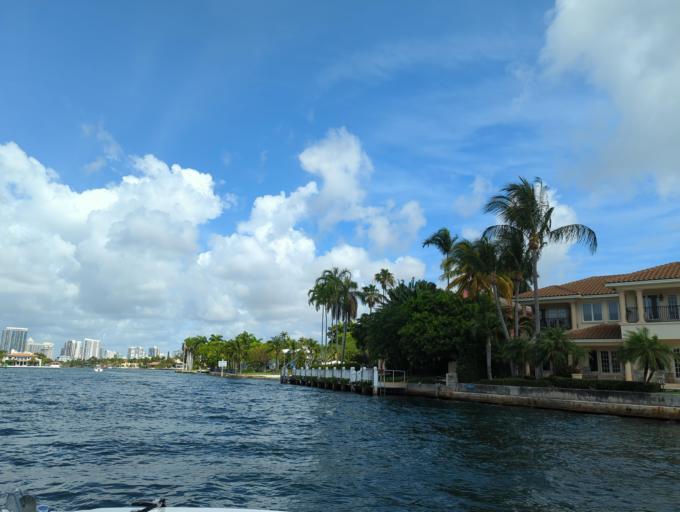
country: US
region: Florida
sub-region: Broward County
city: Sunrise
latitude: 26.1109
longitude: -80.1153
